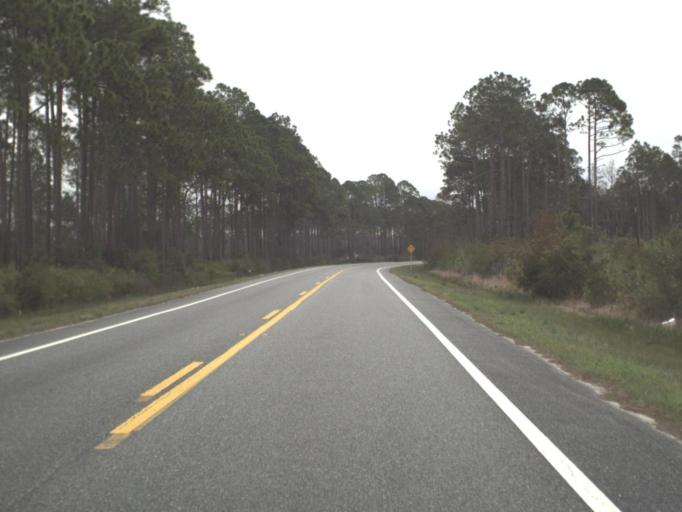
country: US
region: Florida
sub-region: Franklin County
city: Eastpoint
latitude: 29.8286
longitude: -84.8635
